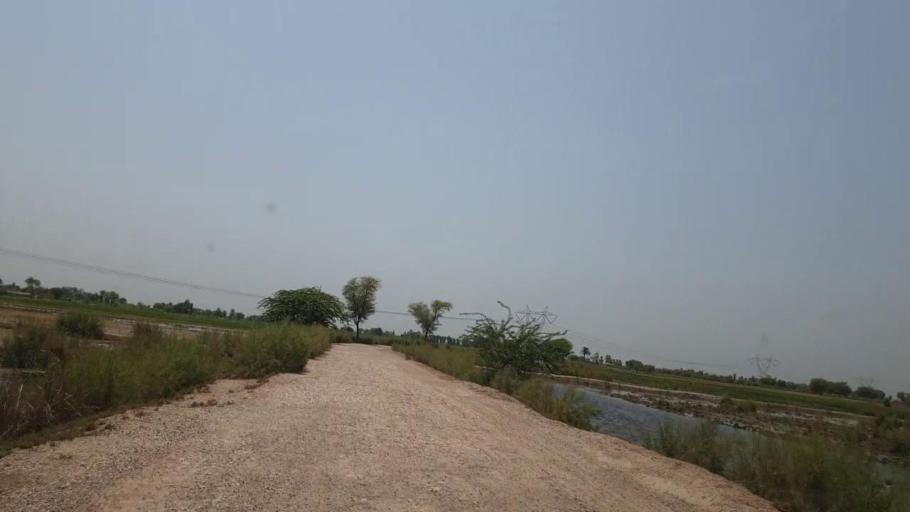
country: PK
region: Sindh
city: Shikarpur
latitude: 27.8918
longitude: 68.6309
